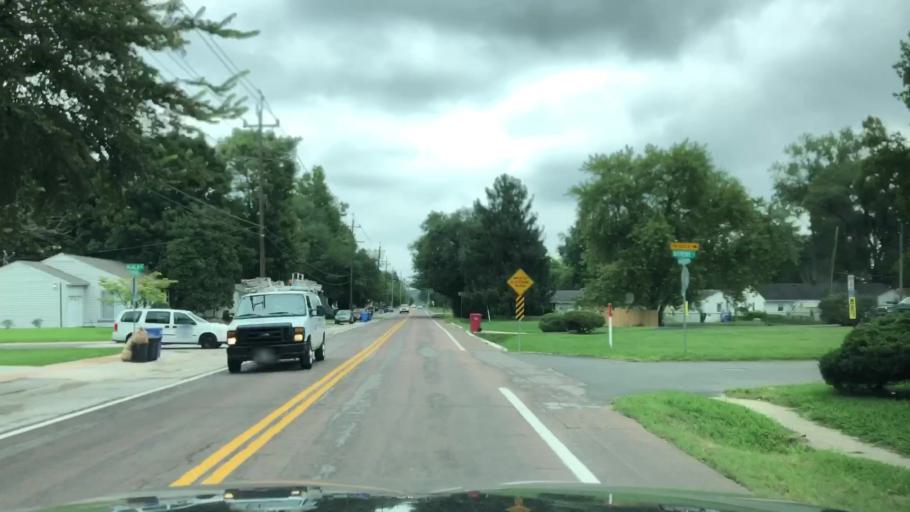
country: US
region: Missouri
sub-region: Saint Louis County
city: Florissant
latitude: 38.8026
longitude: -90.3484
